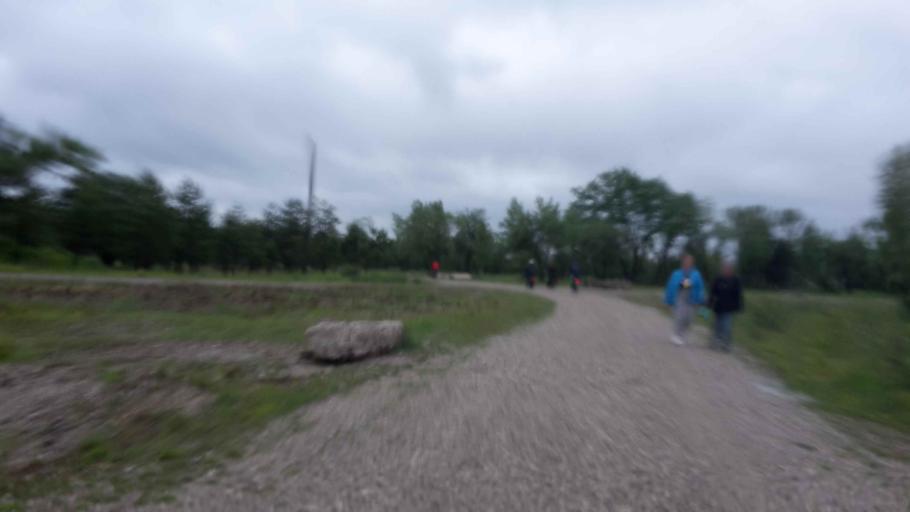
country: DE
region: Bavaria
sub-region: Upper Bavaria
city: Unterfoehring
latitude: 48.2149
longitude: 11.6138
